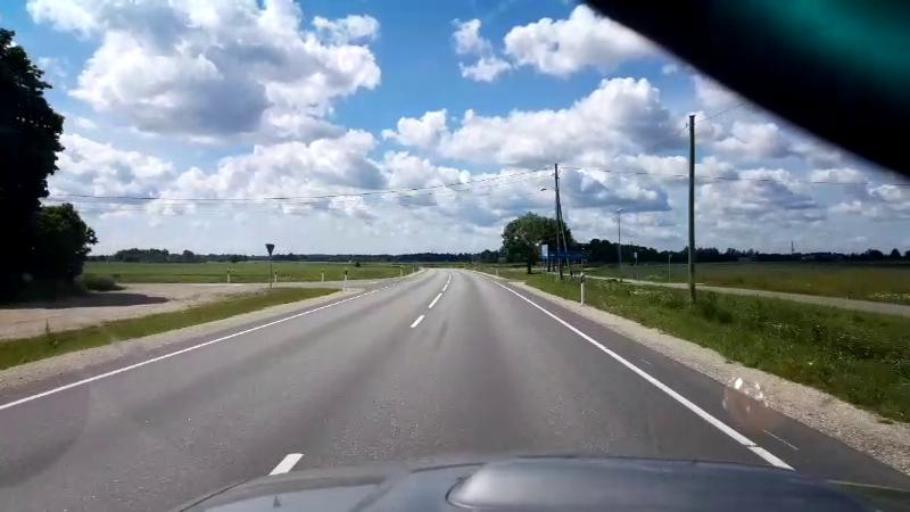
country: EE
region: Jaervamaa
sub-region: Jaerva-Jaani vald
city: Jarva-Jaani
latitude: 59.0968
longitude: 25.6970
